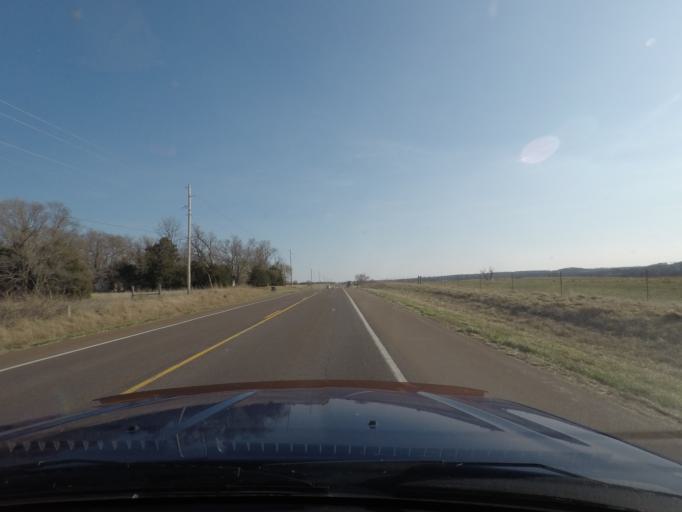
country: US
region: Kansas
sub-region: Douglas County
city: Lawrence
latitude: 39.0275
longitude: -95.3913
